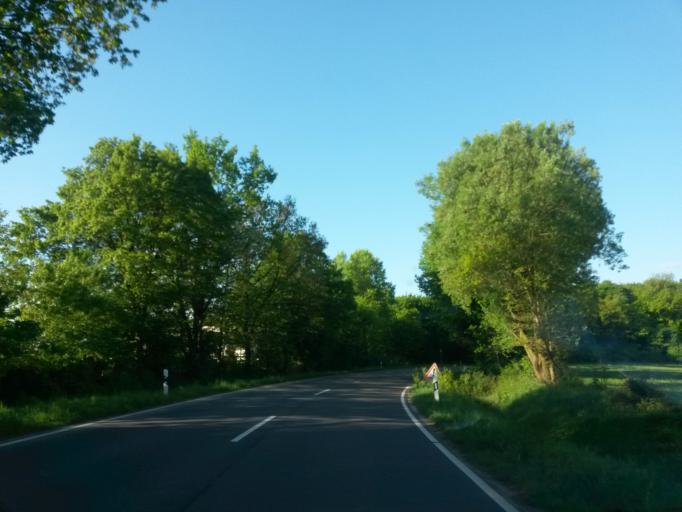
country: DE
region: North Rhine-Westphalia
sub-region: Regierungsbezirk Koln
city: Numbrecht
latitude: 50.9179
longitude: 7.4939
